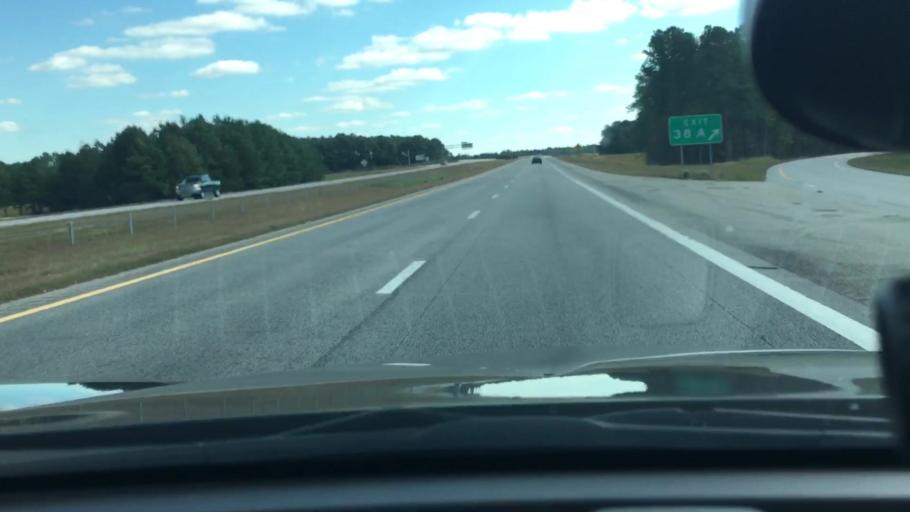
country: US
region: North Carolina
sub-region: Wilson County
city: Lucama
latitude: 35.7382
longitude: -78.0153
